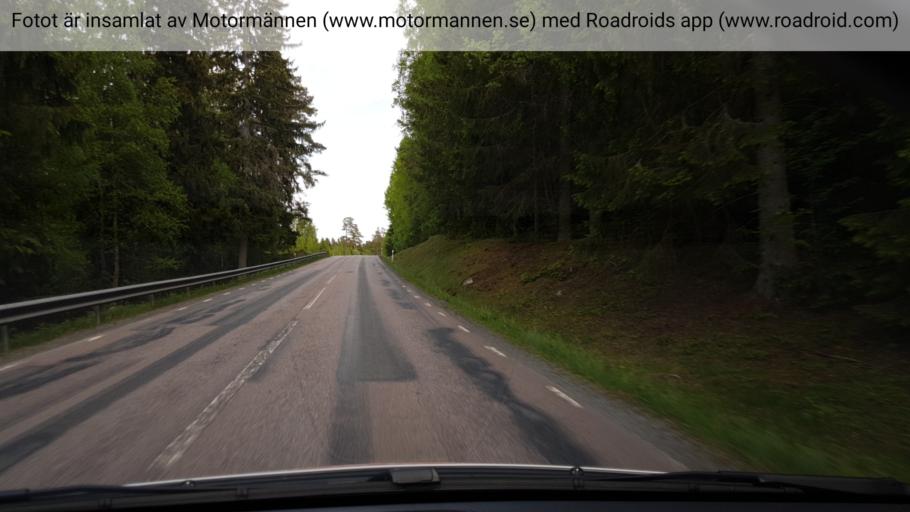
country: SE
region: Vaestmanland
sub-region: Kopings Kommun
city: Kolsva
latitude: 59.6440
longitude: 15.7905
